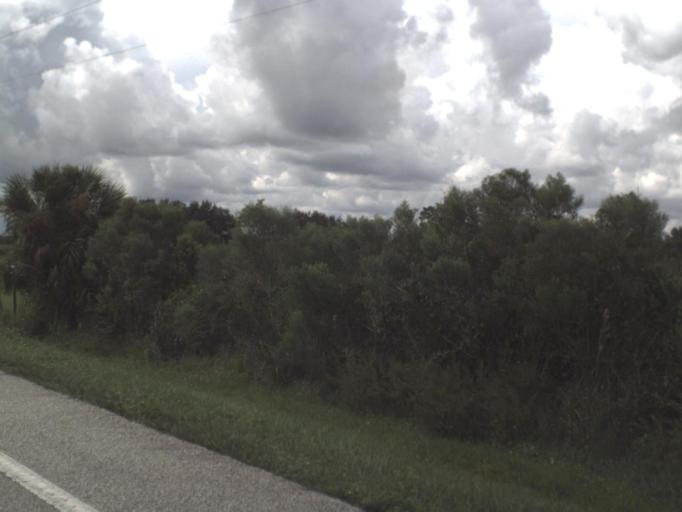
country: US
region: Florida
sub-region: DeSoto County
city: Nocatee
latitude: 27.2040
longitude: -82.0572
